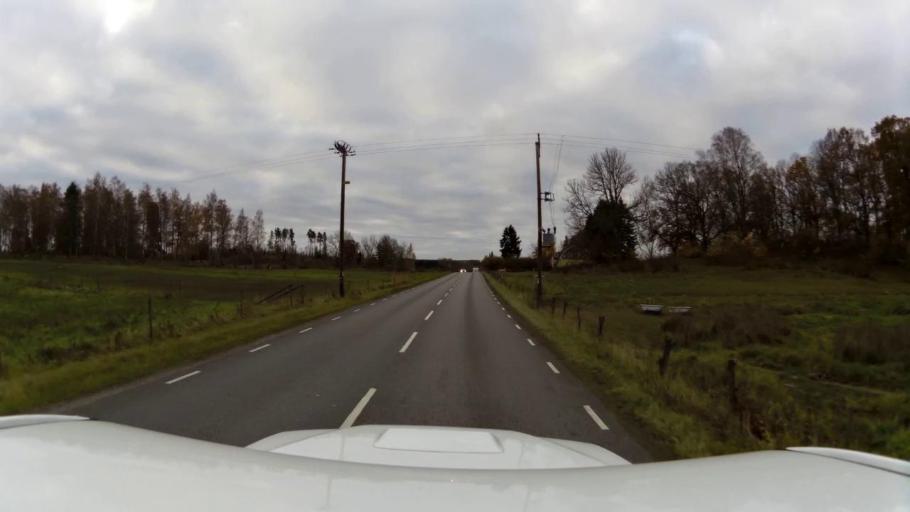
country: SE
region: OEstergoetland
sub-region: Linkopings Kommun
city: Linghem
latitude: 58.4073
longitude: 15.7647
